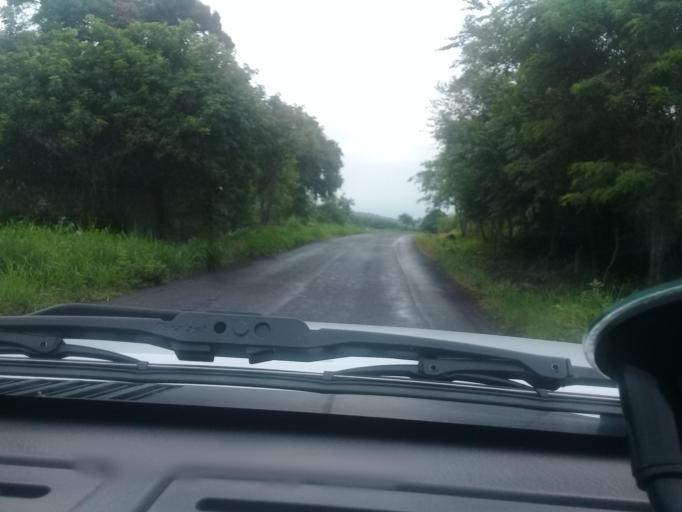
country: MX
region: Veracruz
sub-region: Paso de Ovejas
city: Tolome
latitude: 19.2569
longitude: -96.4242
